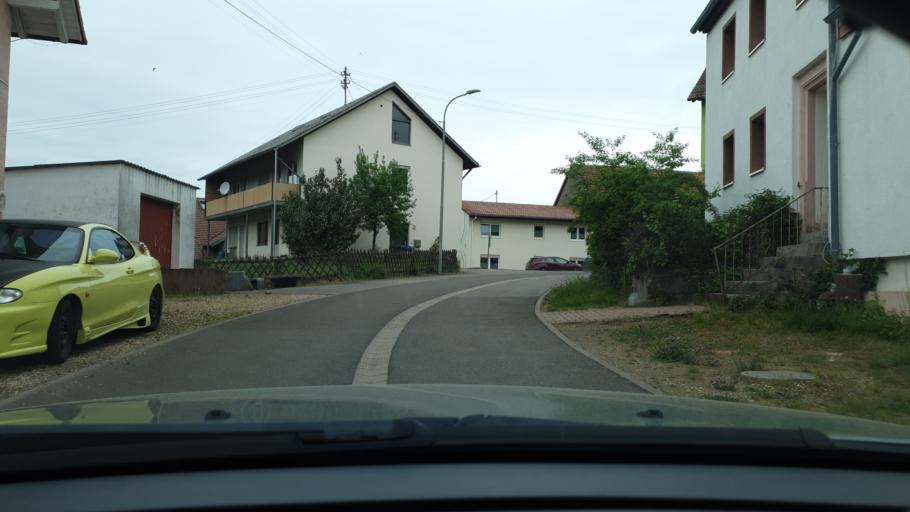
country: DE
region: Rheinland-Pfalz
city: Langwieden
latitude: 49.3759
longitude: 7.4987
